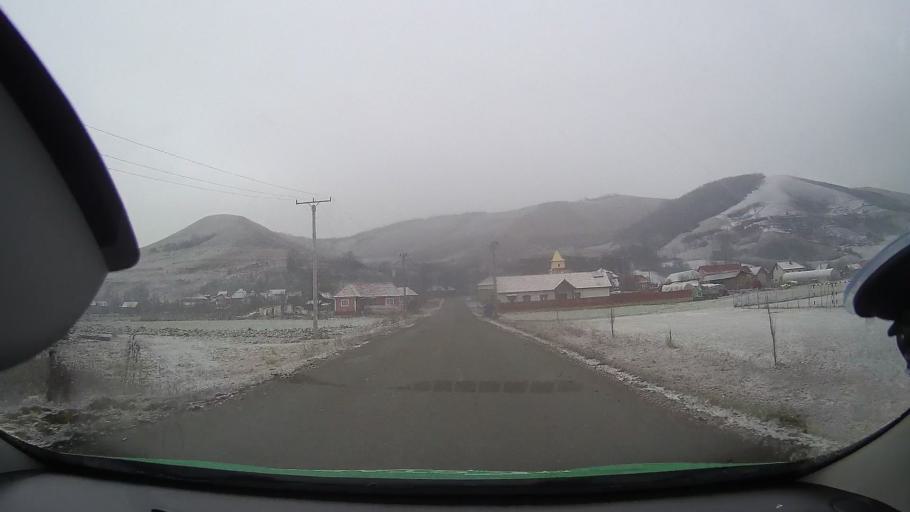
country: RO
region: Alba
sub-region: Comuna Noslac
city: Noslac
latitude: 46.3484
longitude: 23.9349
